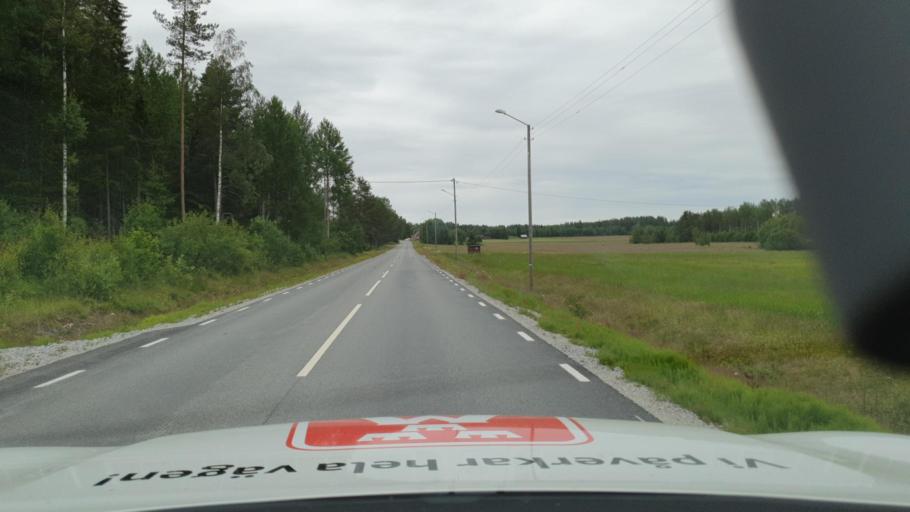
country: SE
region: Vaesterbotten
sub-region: Nordmalings Kommun
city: Nordmaling
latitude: 63.5092
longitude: 19.3370
